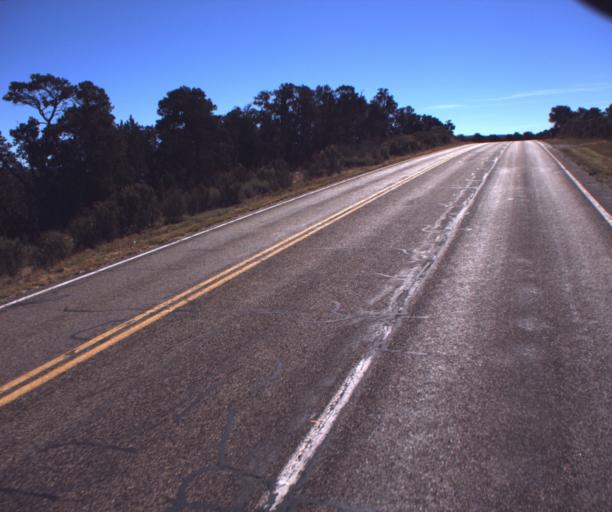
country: US
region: Arizona
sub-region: Coconino County
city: Fredonia
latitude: 36.8045
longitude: -112.2547
